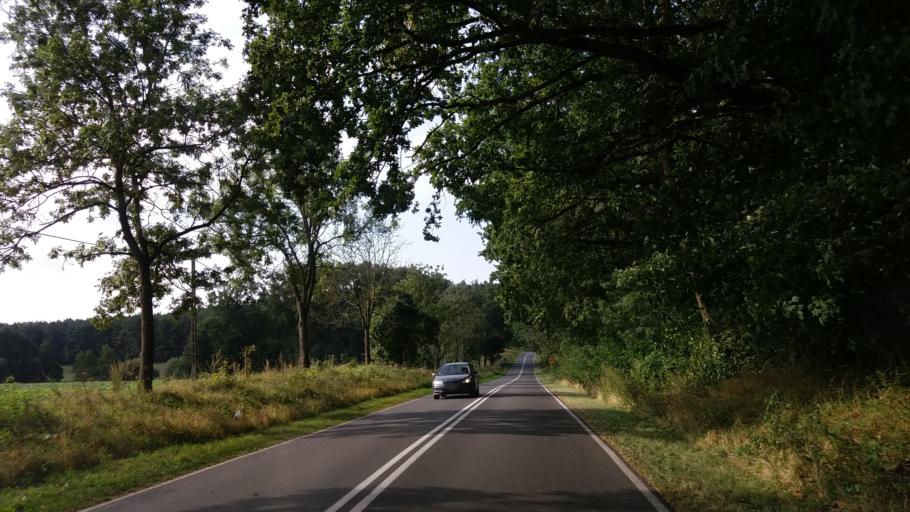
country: PL
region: West Pomeranian Voivodeship
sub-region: Powiat stargardzki
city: Suchan
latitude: 53.2434
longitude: 15.3229
